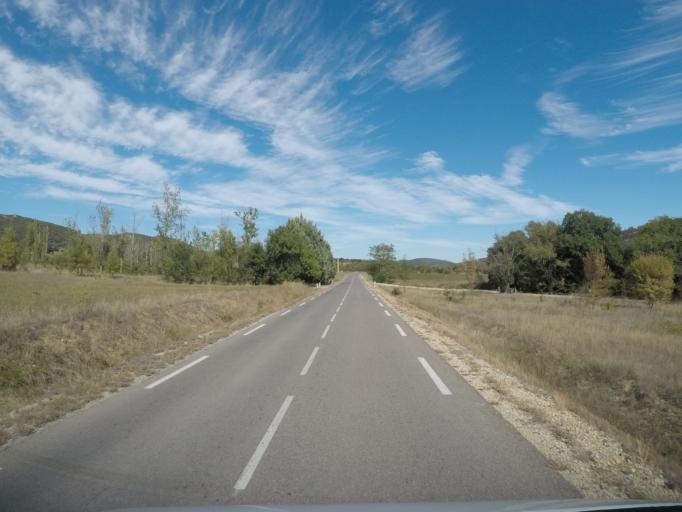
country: FR
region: Languedoc-Roussillon
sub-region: Departement de l'Herault
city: Saint-Bauzille-de-Putois
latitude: 43.9156
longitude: 3.7780
